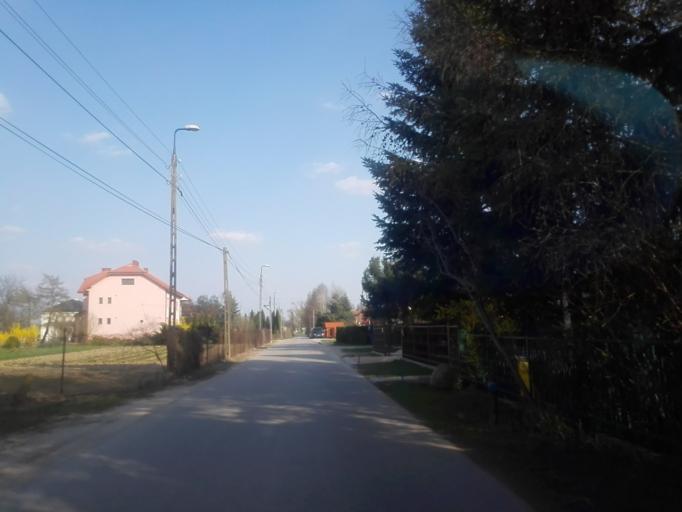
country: PL
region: Masovian Voivodeship
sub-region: Powiat piaseczynski
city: Konstancin-Jeziorna
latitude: 52.1390
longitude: 21.1440
